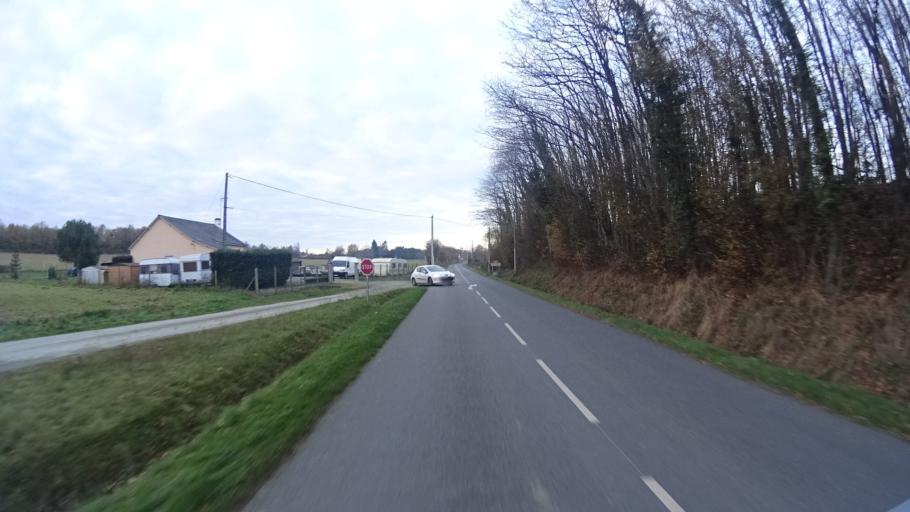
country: FR
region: Brittany
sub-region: Departement d'Ille-et-Vilaine
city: Langon
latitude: 47.6738
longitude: -1.9052
